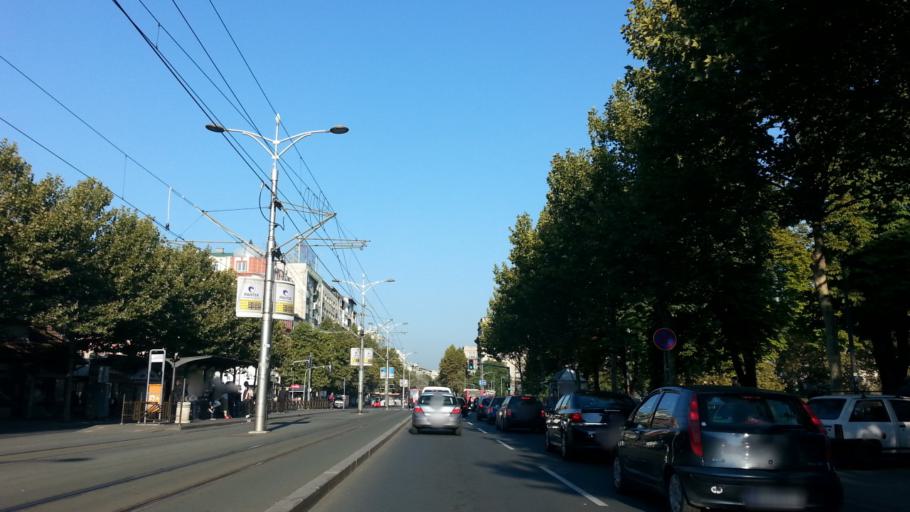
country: RS
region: Central Serbia
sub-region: Belgrade
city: Vracar
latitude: 44.8040
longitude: 20.4791
